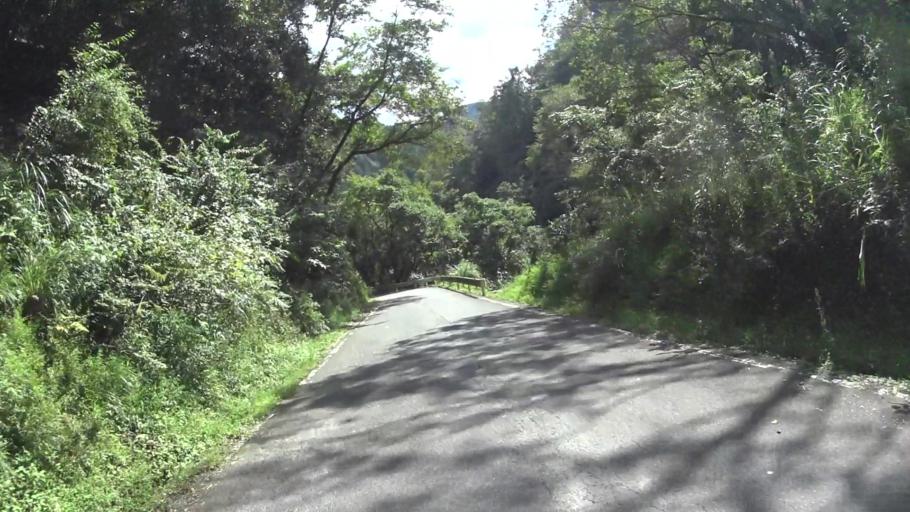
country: JP
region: Kyoto
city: Uji
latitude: 34.9081
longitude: 135.8667
